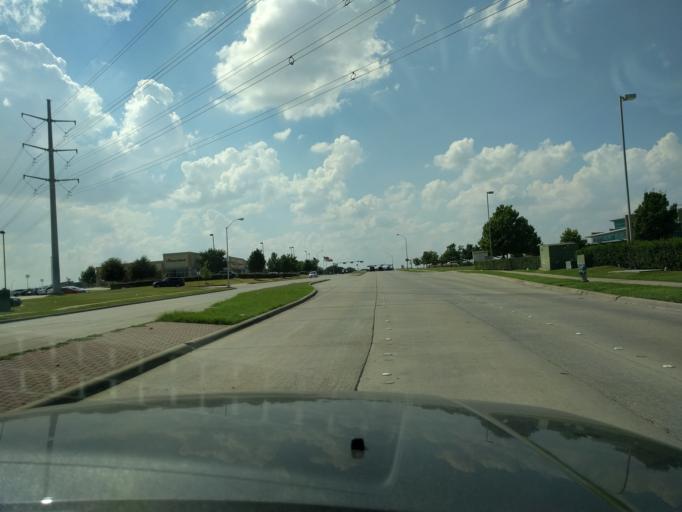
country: US
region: Texas
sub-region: Collin County
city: Allen
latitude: 33.0684
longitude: -96.6957
